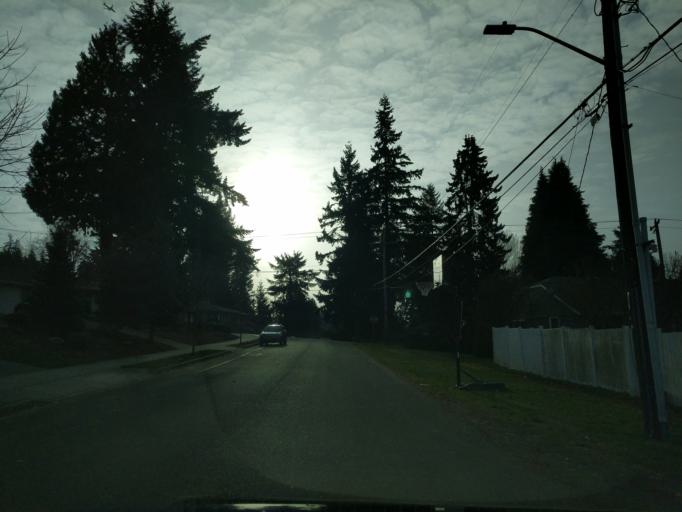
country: US
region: Washington
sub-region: King County
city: Shoreline
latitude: 47.7510
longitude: -122.3276
